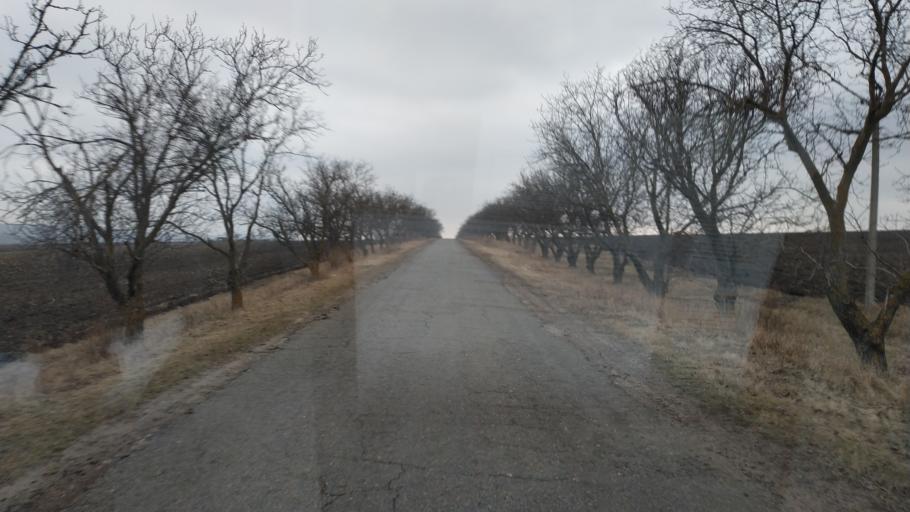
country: MD
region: Hincesti
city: Dancu
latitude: 46.8718
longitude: 28.2948
